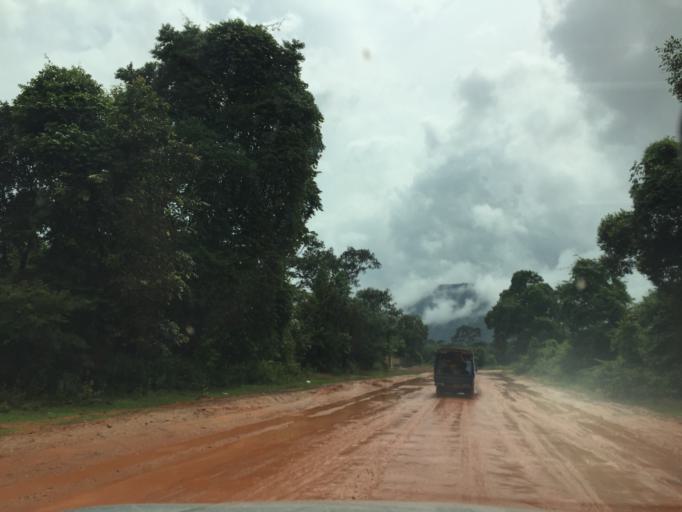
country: LA
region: Attapu
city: Attapu
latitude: 14.8079
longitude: 106.7716
